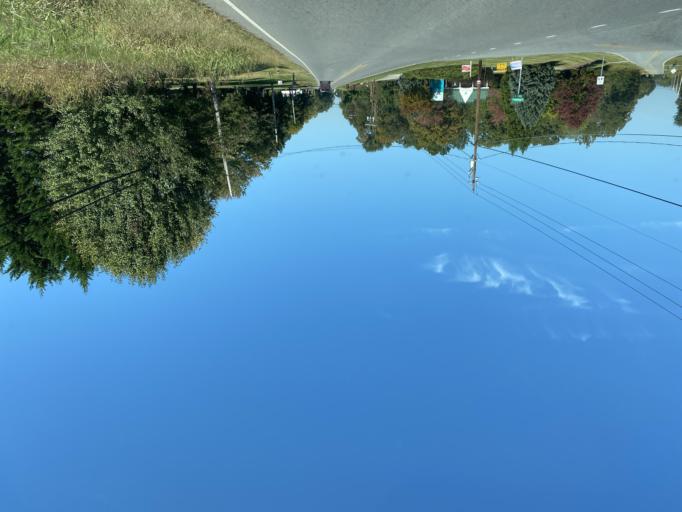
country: US
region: North Carolina
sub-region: Cleveland County
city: Boiling Springs
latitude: 35.2671
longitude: -81.6674
